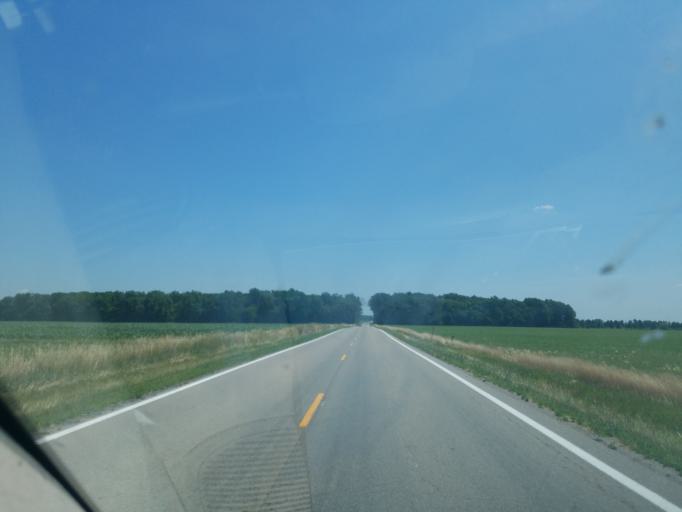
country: US
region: Ohio
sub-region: Allen County
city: Spencerville
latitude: 40.7428
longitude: -84.4407
